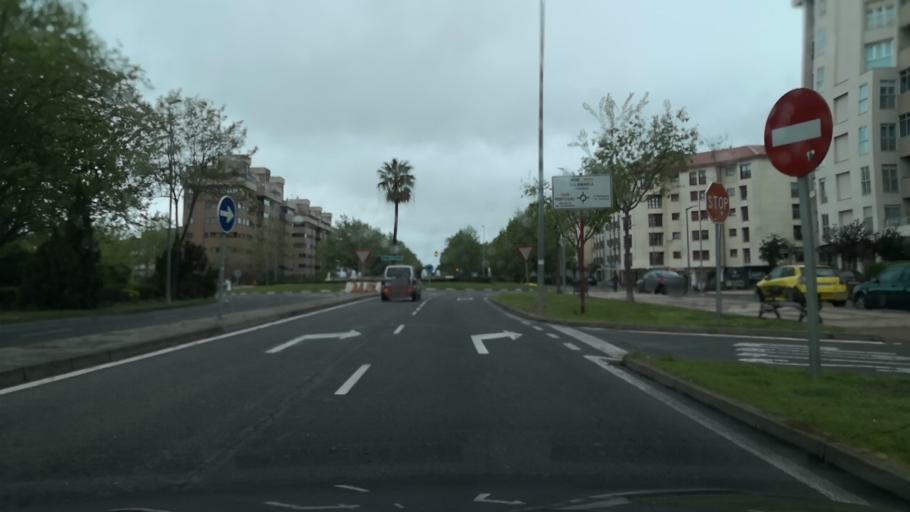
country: ES
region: Extremadura
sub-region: Provincia de Caceres
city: Caceres
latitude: 39.4710
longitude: -6.3876
